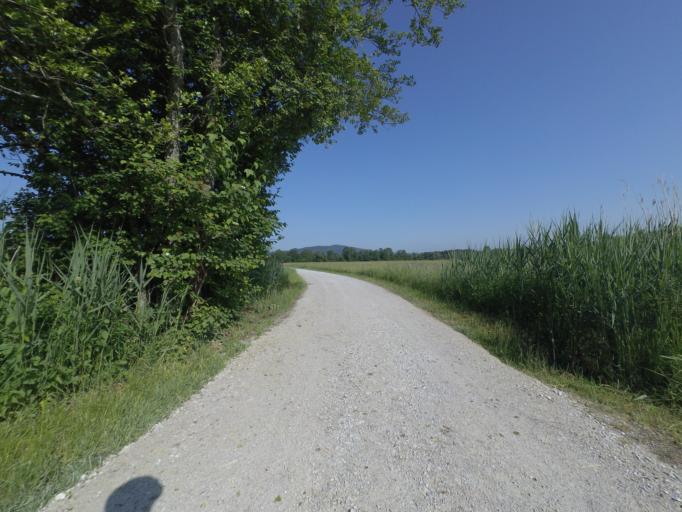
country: AT
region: Salzburg
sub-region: Politischer Bezirk Salzburg-Umgebung
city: Grodig
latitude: 47.7599
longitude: 12.9827
